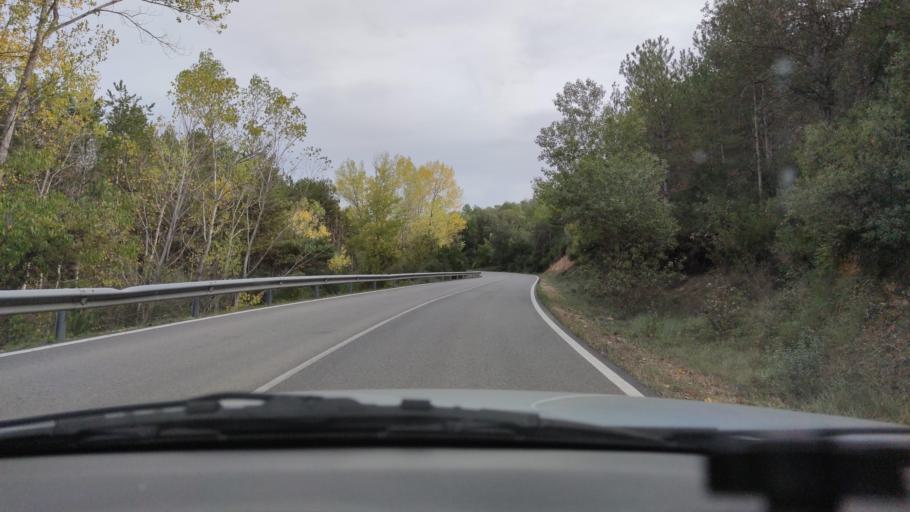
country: ES
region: Catalonia
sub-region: Provincia de Lleida
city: Artesa de Segre
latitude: 41.9355
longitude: 1.0536
